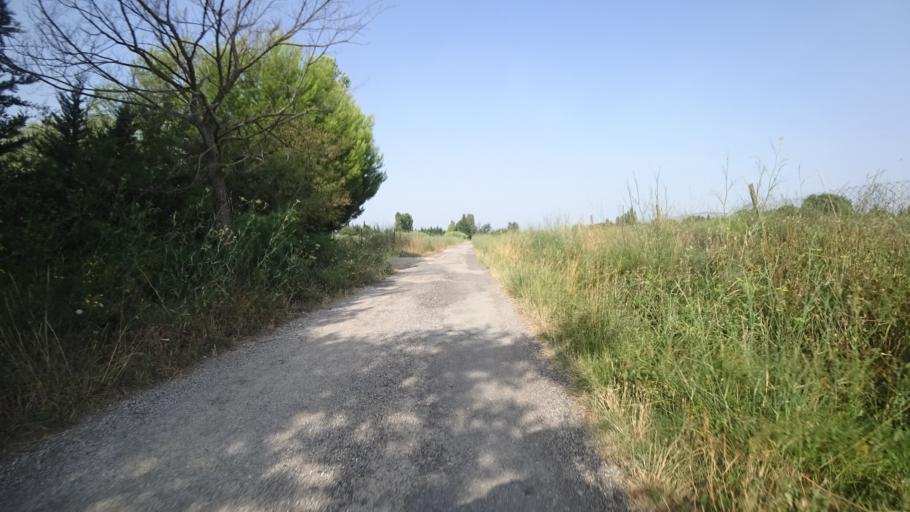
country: FR
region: Languedoc-Roussillon
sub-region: Departement des Pyrenees-Orientales
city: Torreilles
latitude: 42.7346
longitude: 3.0036
